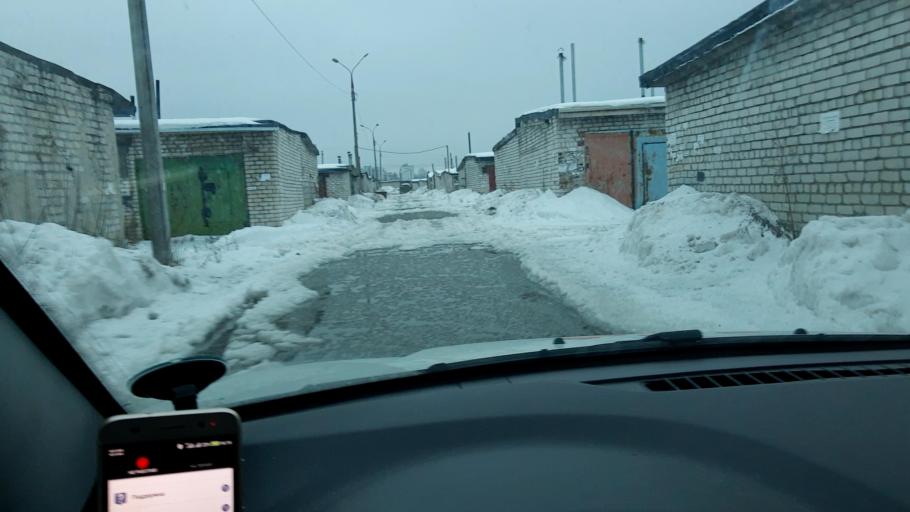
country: RU
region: Nizjnij Novgorod
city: Gorbatovka
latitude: 56.2528
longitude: 43.8294
